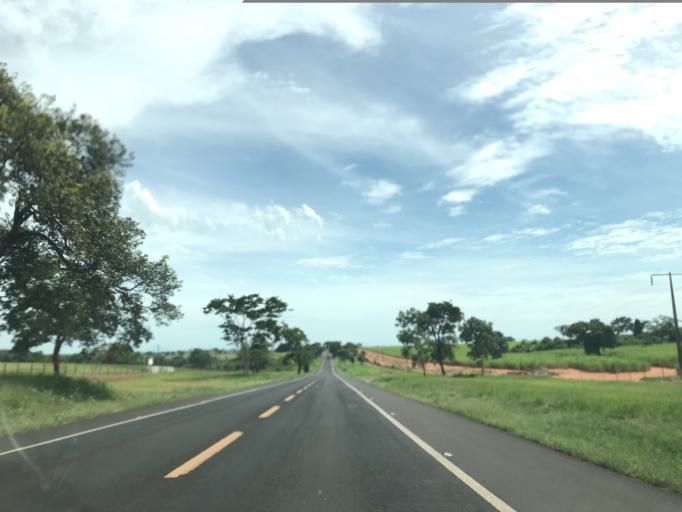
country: BR
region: Sao Paulo
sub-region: Nova Granada
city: Nova Granada
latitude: -20.3615
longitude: -49.2196
